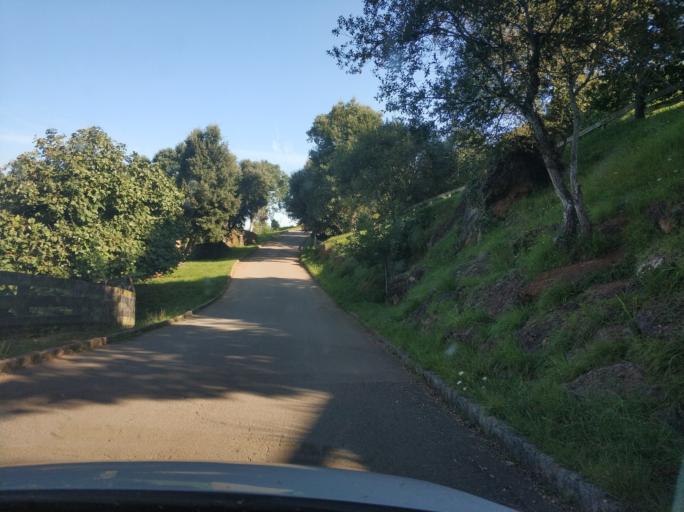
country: ES
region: Cantabria
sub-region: Provincia de Cantabria
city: Santa Maria de Cayon
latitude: 43.3447
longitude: -3.8565
